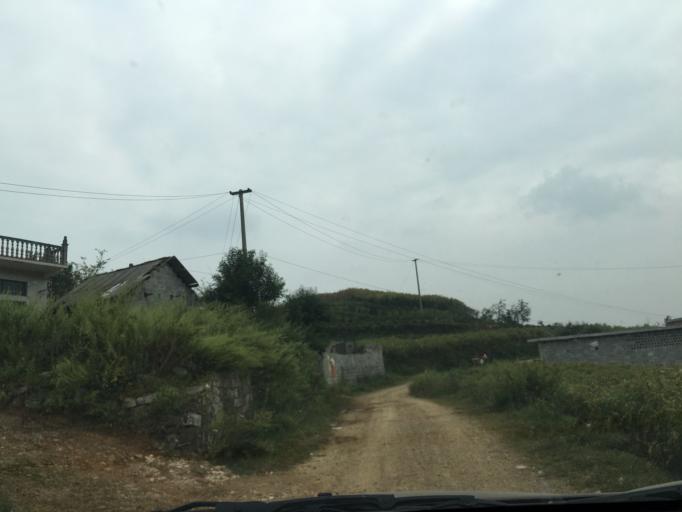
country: CN
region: Guangxi Zhuangzu Zizhiqu
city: Xinzhou
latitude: 25.5403
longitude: 105.5313
